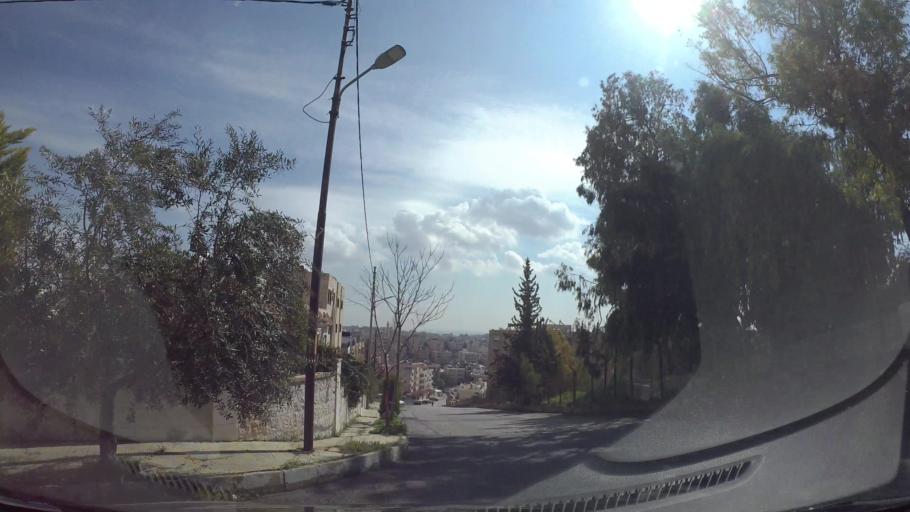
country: JO
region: Amman
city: Al Jubayhah
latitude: 31.9924
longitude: 35.8994
